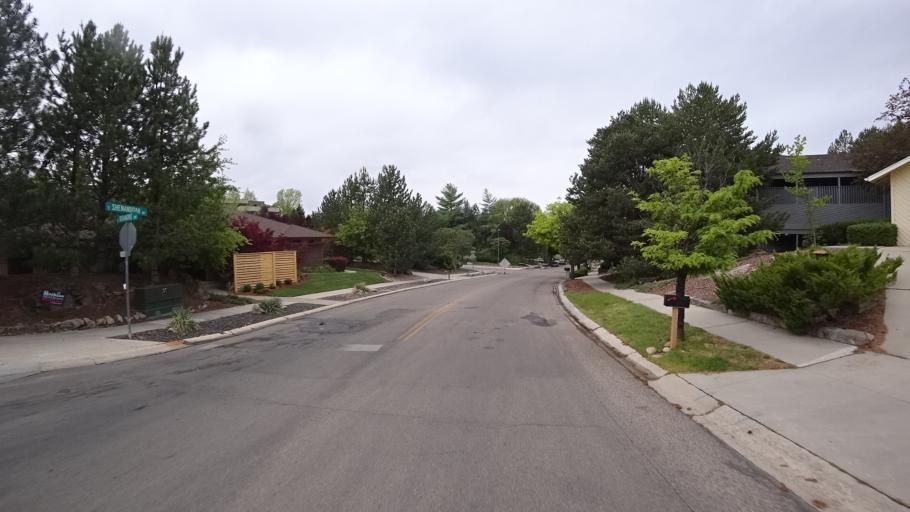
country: US
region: Idaho
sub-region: Ada County
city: Boise
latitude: 43.6121
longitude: -116.1707
